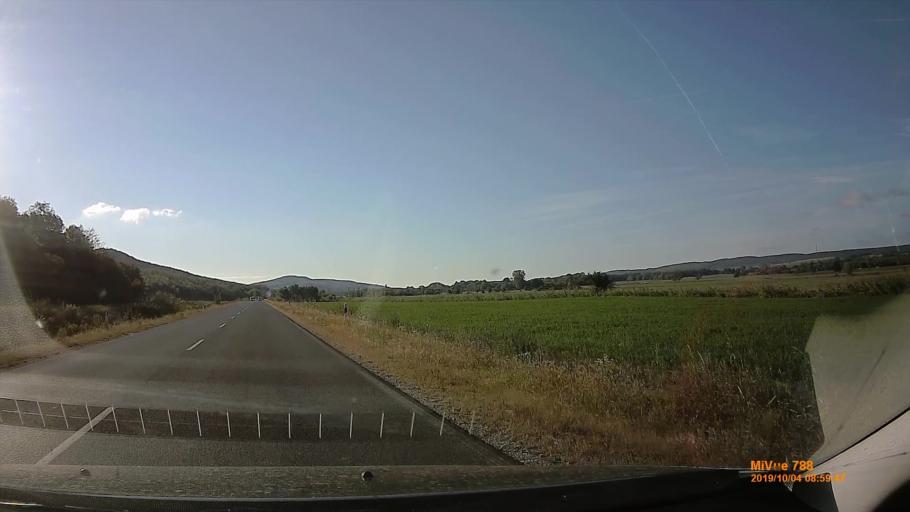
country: HU
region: Somogy
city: Balatonlelle
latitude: 46.7563
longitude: 17.7659
